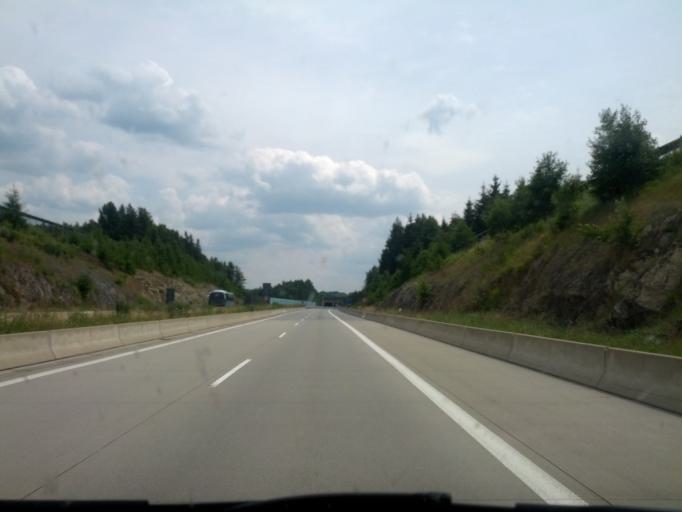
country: DE
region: Saxony
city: Liebstadt
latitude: 50.7927
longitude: 13.8870
